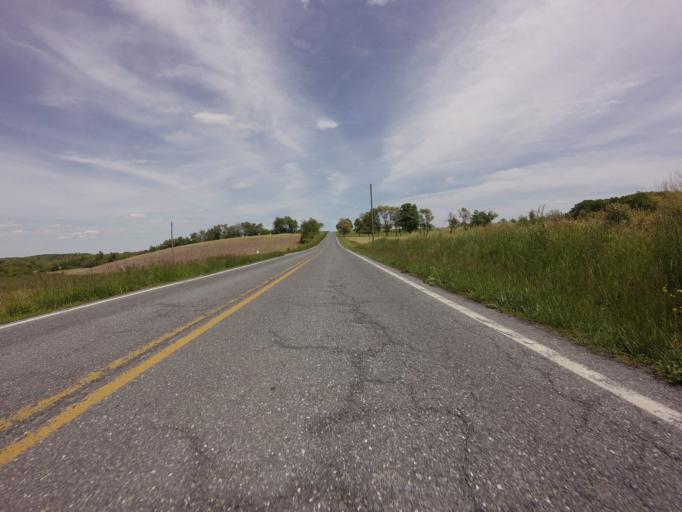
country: US
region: Maryland
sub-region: Frederick County
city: Woodsboro
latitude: 39.5151
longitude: -77.2412
